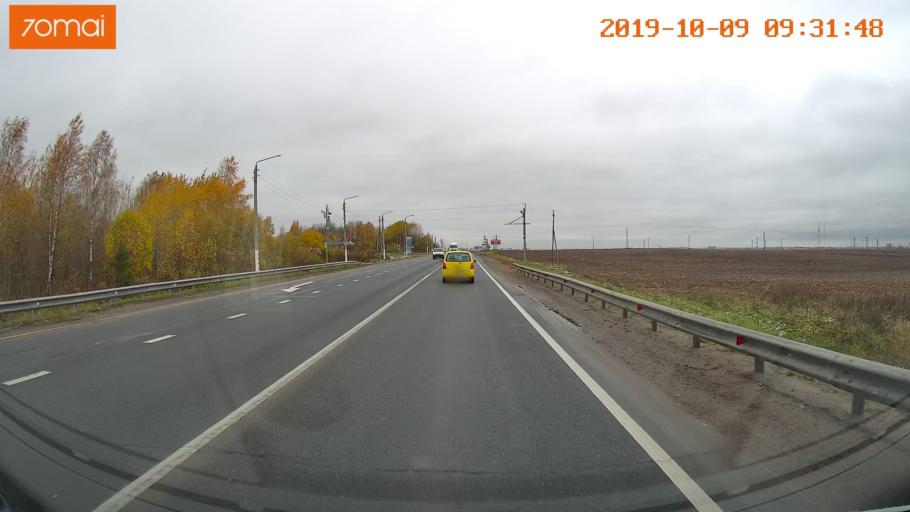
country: RU
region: Vologda
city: Vologda
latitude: 59.1528
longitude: 39.9350
